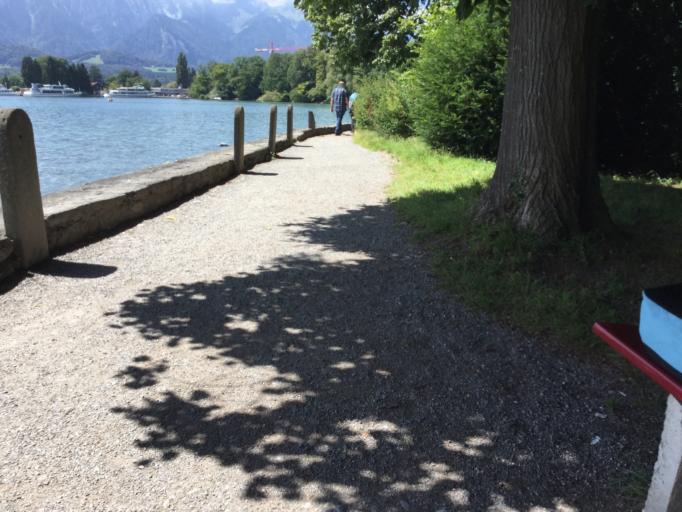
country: CH
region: Bern
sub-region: Thun District
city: Thun
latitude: 46.7449
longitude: 7.6365
